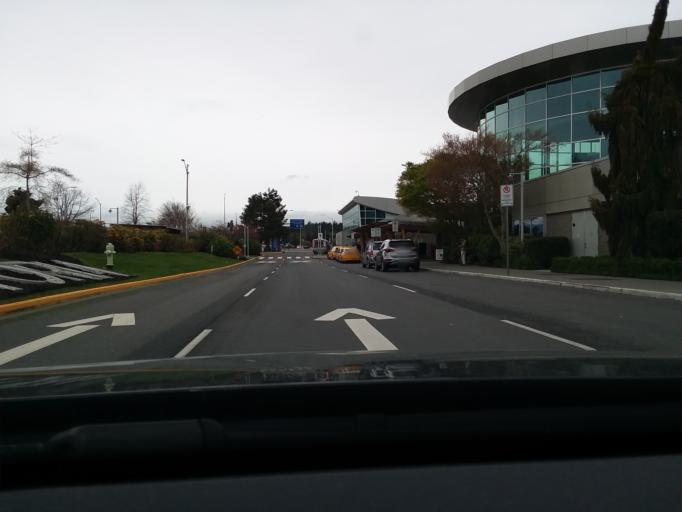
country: CA
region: British Columbia
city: North Saanich
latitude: 48.6402
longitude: -123.4302
